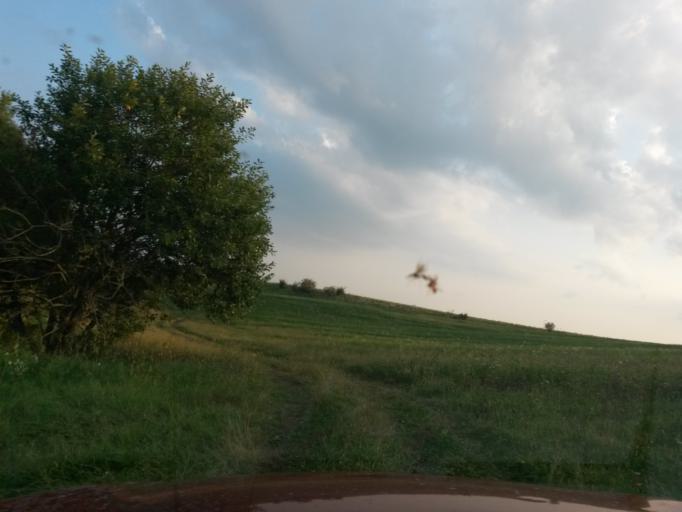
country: SK
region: Kosicky
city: Secovce
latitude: 48.8048
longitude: 21.4722
